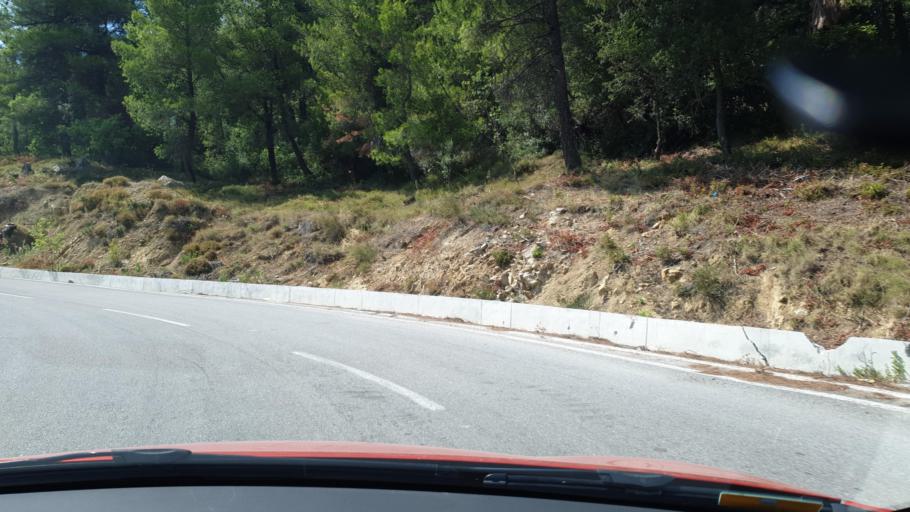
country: GR
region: Central Greece
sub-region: Nomos Evvoias
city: Politika
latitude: 38.6443
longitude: 23.5654
